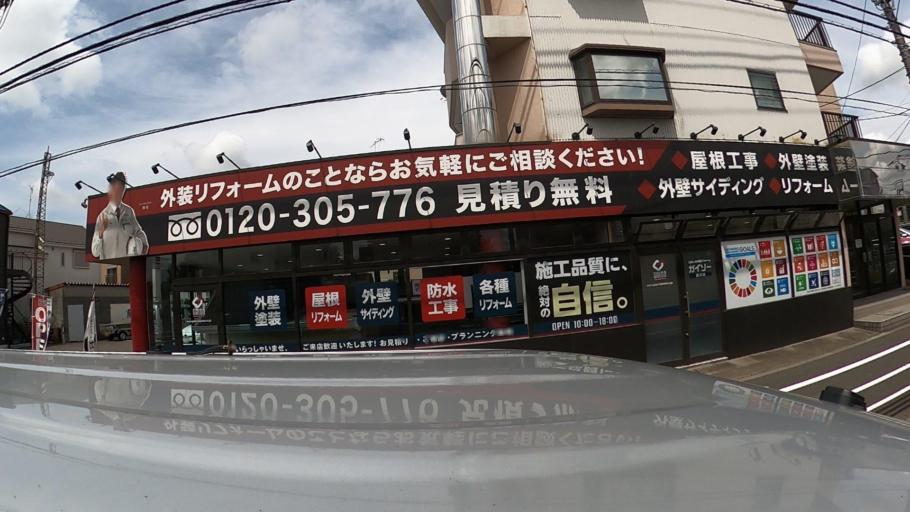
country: JP
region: Kanagawa
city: Fujisawa
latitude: 35.4085
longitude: 139.4698
